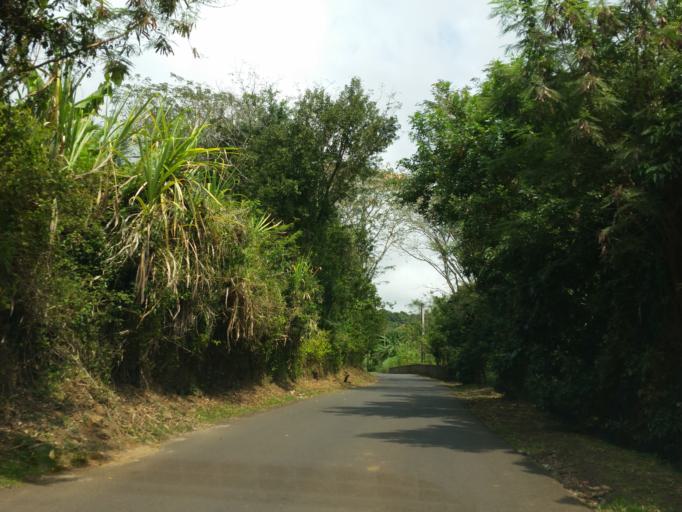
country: RE
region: Reunion
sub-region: Reunion
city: Sainte-Suzanne
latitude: -20.9218
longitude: 55.6105
